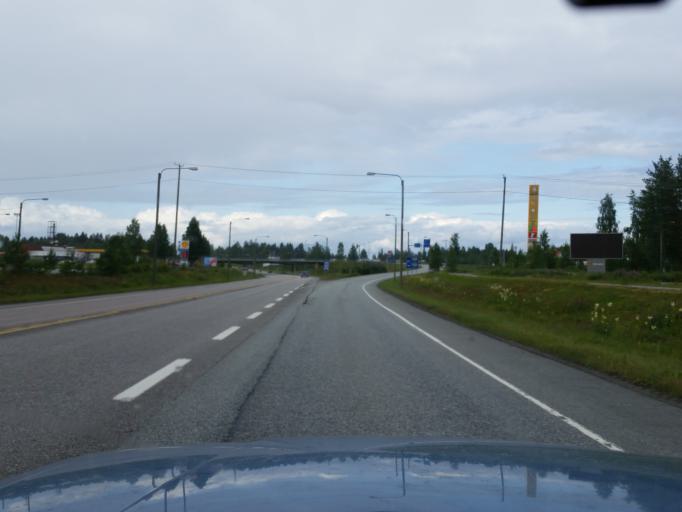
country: FI
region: Southern Savonia
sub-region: Pieksaemaeki
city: Juva
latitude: 61.8957
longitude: 27.8012
